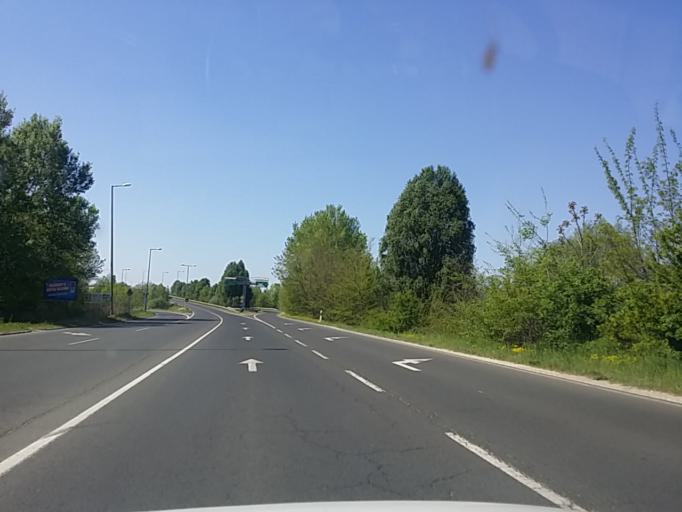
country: HU
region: Budapest
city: Budapest XV. keruelet
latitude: 47.5853
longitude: 19.1549
